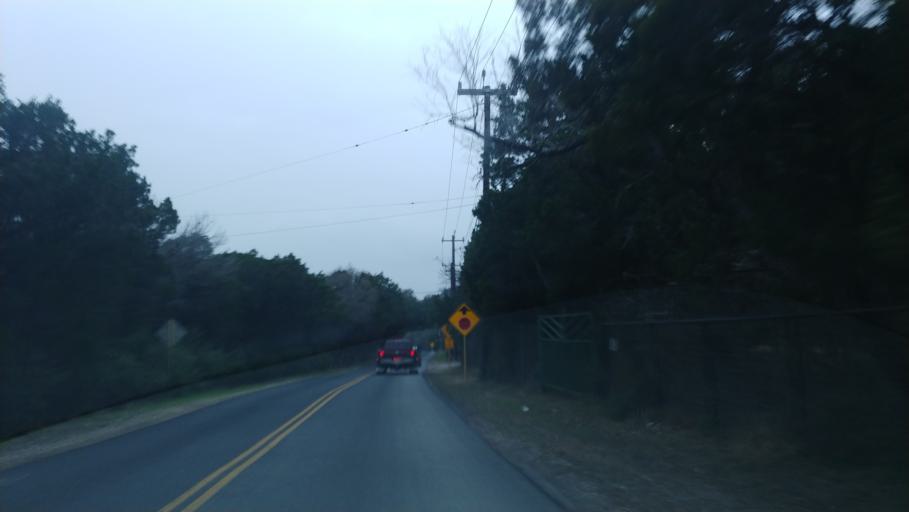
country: US
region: Texas
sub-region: Bexar County
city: Helotes
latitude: 29.6078
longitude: -98.6850
